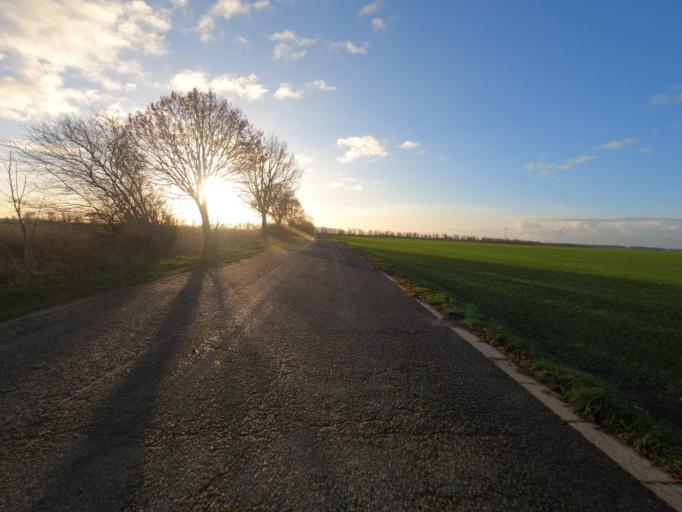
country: DE
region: North Rhine-Westphalia
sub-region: Regierungsbezirk Koln
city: Titz
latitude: 51.0026
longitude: 6.3882
